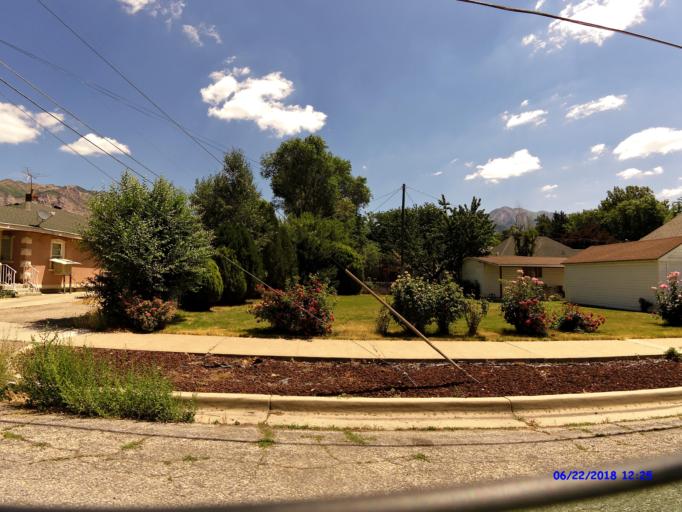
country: US
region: Utah
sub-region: Weber County
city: Ogden
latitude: 41.2381
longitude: -111.9645
